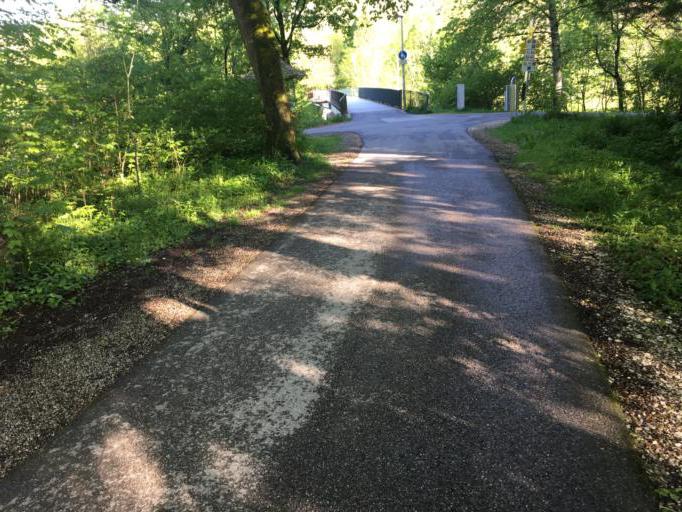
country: DE
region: Bavaria
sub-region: Upper Bavaria
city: Bad Reichenhall
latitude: 47.7319
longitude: 12.8711
